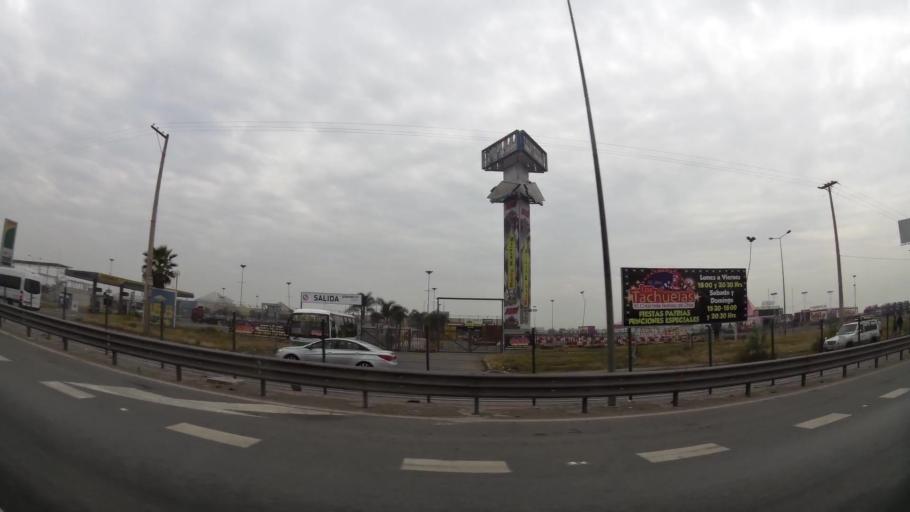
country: CL
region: Santiago Metropolitan
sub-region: Provincia de Maipo
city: San Bernardo
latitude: -33.5189
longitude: -70.7073
